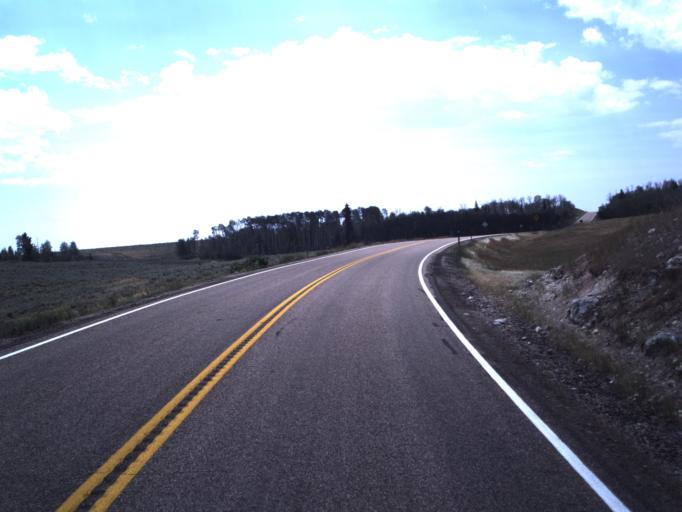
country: US
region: Utah
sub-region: Uintah County
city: Maeser
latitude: 40.6992
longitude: -109.4920
